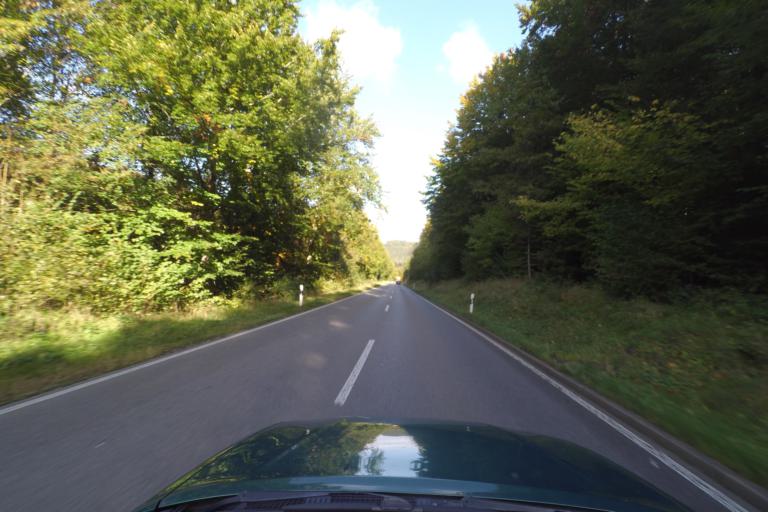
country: DE
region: Baden-Wuerttemberg
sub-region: Karlsruhe Region
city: Neubulach
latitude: 48.6712
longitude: 8.6978
